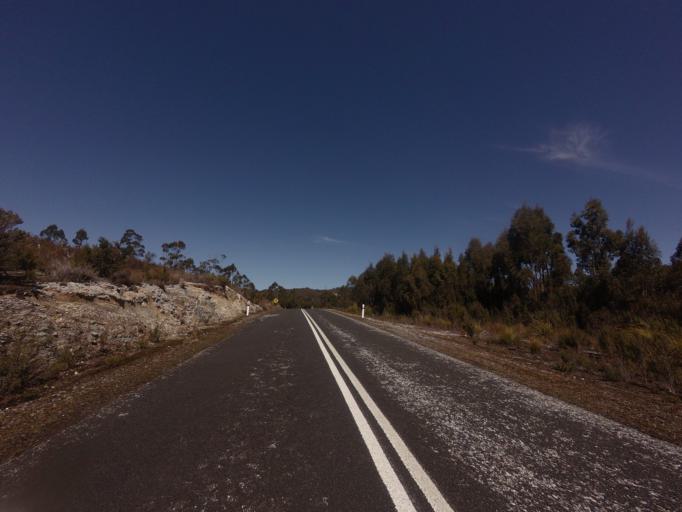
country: AU
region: Tasmania
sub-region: West Coast
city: Queenstown
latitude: -42.7997
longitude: 146.0912
